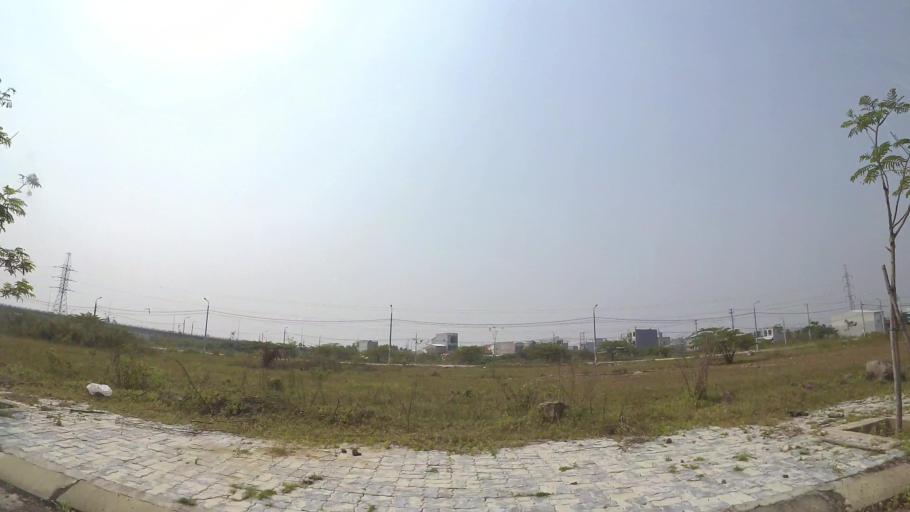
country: VN
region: Da Nang
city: Cam Le
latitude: 15.9706
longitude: 108.2147
